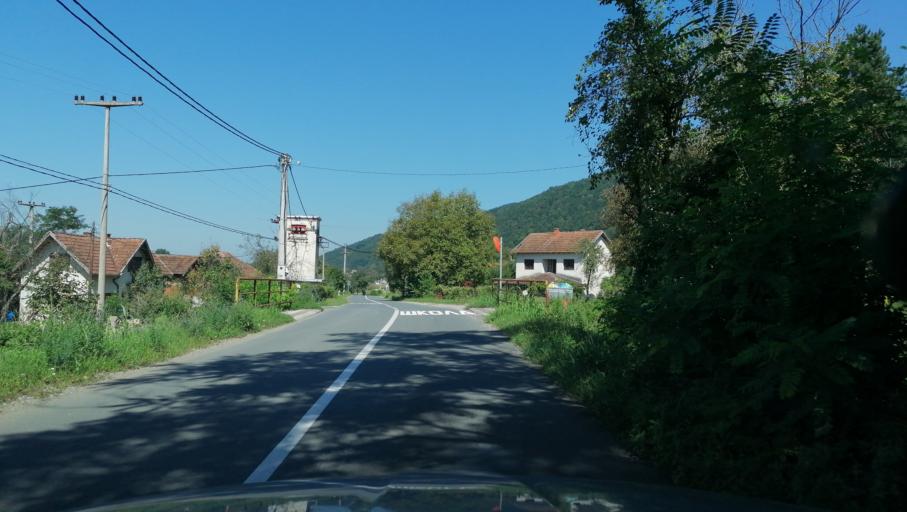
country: RS
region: Central Serbia
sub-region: Raski Okrug
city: Vrnjacka Banja
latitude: 43.6541
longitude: 20.9358
